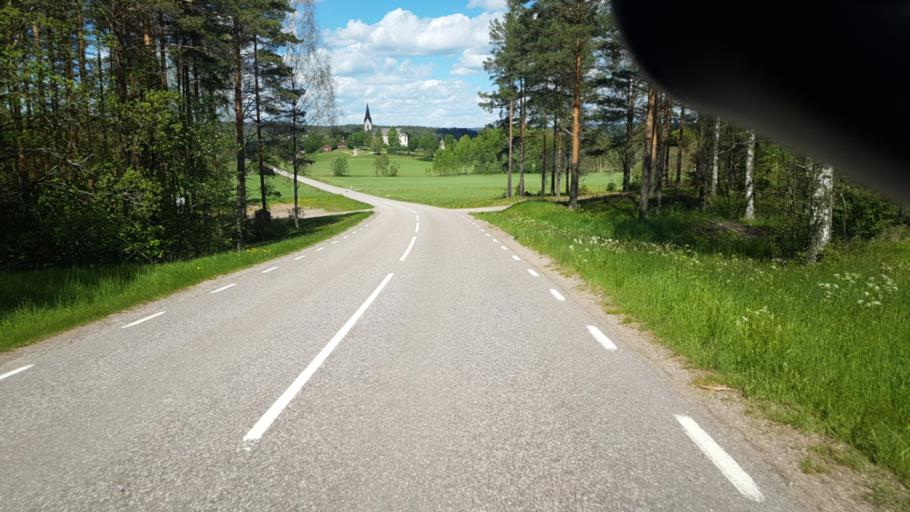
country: SE
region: Vaermland
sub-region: Arvika Kommun
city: Arvika
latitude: 59.6466
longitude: 12.8931
